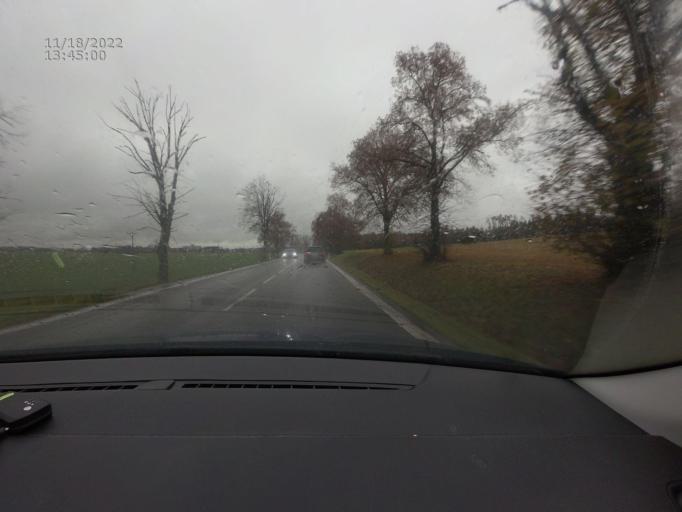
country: CZ
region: Jihocesky
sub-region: Okres Strakonice
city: Blatna
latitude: 49.4296
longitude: 13.8394
